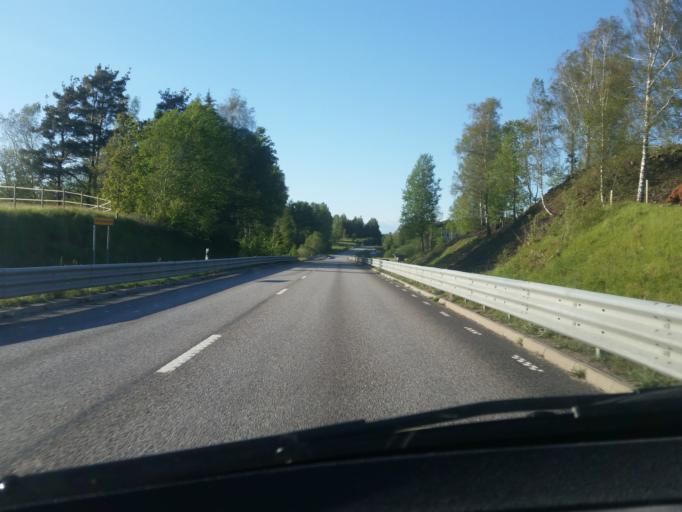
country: SE
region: Vaestra Goetaland
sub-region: Fargelanda Kommun
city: Faergelanda
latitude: 58.5524
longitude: 11.9929
